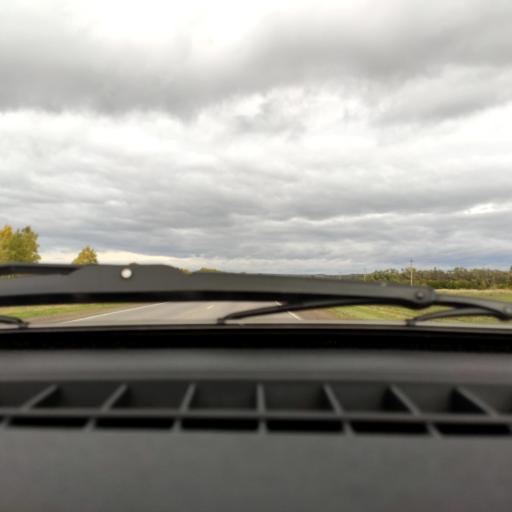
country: RU
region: Bashkortostan
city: Rayevskiy
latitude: 54.0214
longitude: 54.8861
